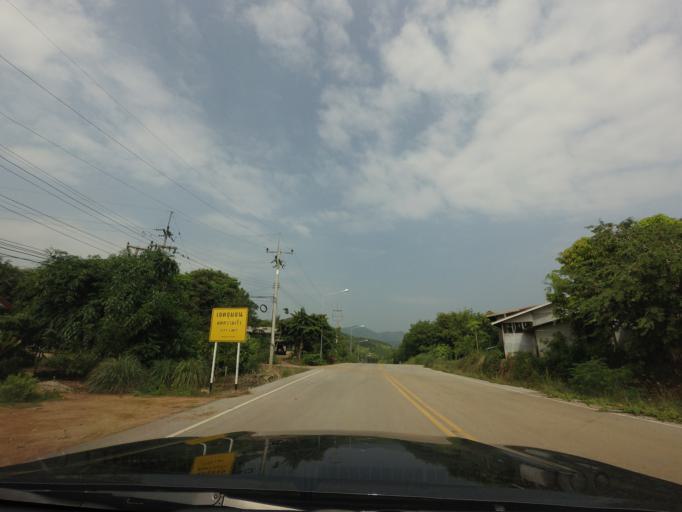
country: TH
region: Loei
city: Chiang Khan
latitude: 17.7797
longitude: 101.5775
